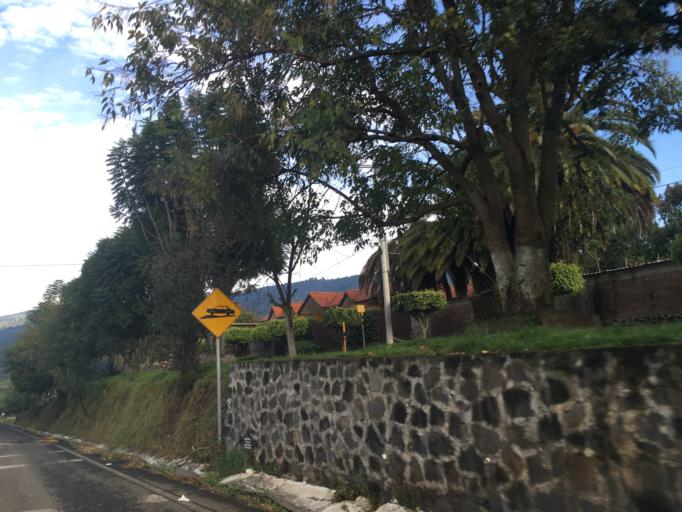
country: MX
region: Michoacan
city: Tingambato
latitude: 19.5058
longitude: -101.8520
